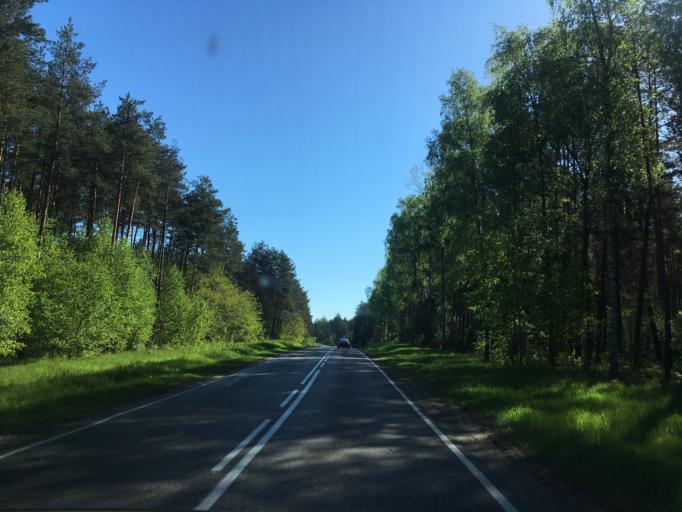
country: PL
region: Warmian-Masurian Voivodeship
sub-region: Powiat szczycienski
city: Jedwabno
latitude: 53.5373
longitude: 20.8216
